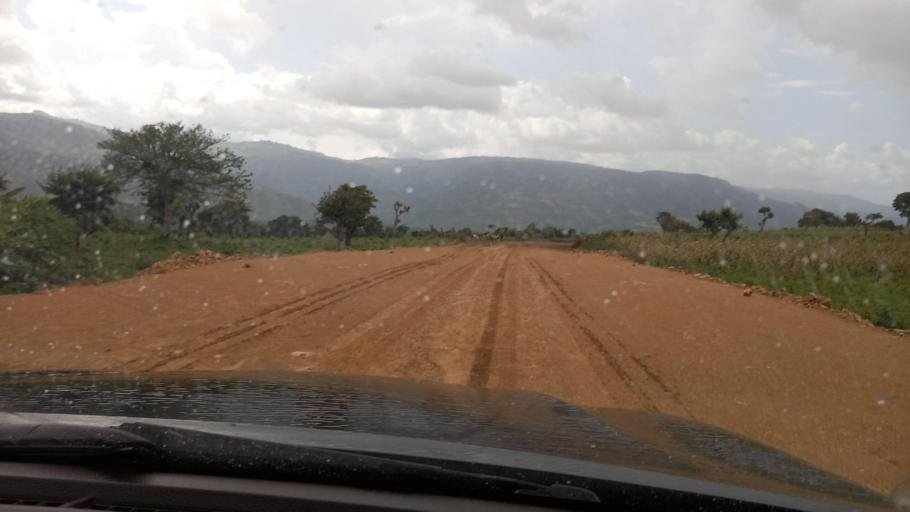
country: ET
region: Southern Nations, Nationalities, and People's Region
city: Mizan Teferi
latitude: 6.1758
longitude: 35.7055
